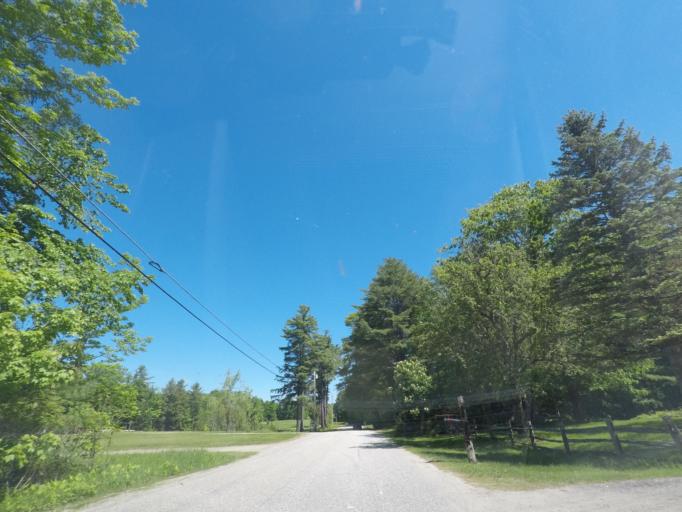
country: US
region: Maine
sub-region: Kennebec County
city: Winthrop
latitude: 44.2619
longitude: -69.9135
